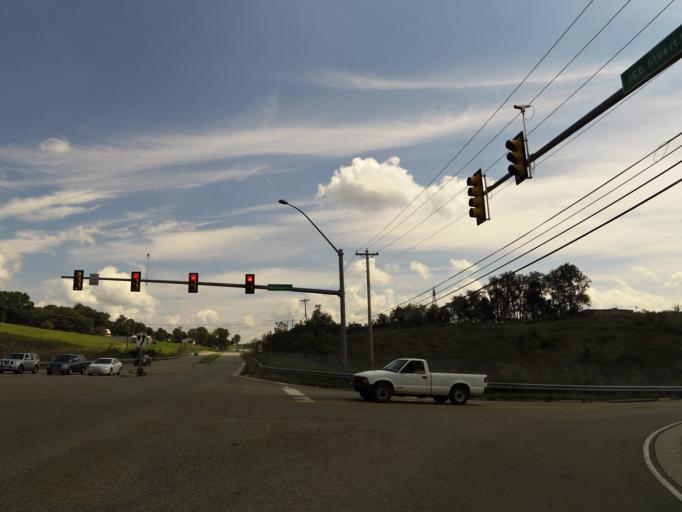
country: US
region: Virginia
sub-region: Washington County
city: Abingdon
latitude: 36.7025
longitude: -81.9145
